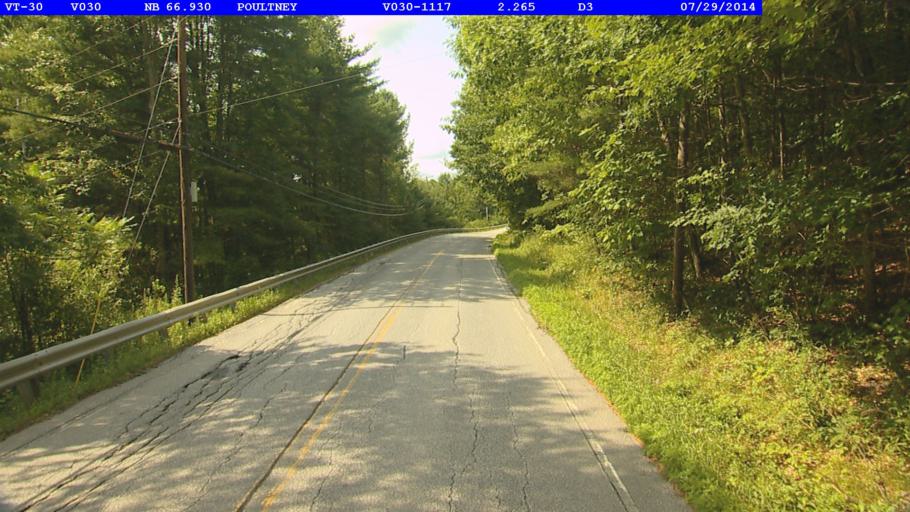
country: US
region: Vermont
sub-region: Rutland County
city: Poultney
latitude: 43.4949
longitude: -73.2055
